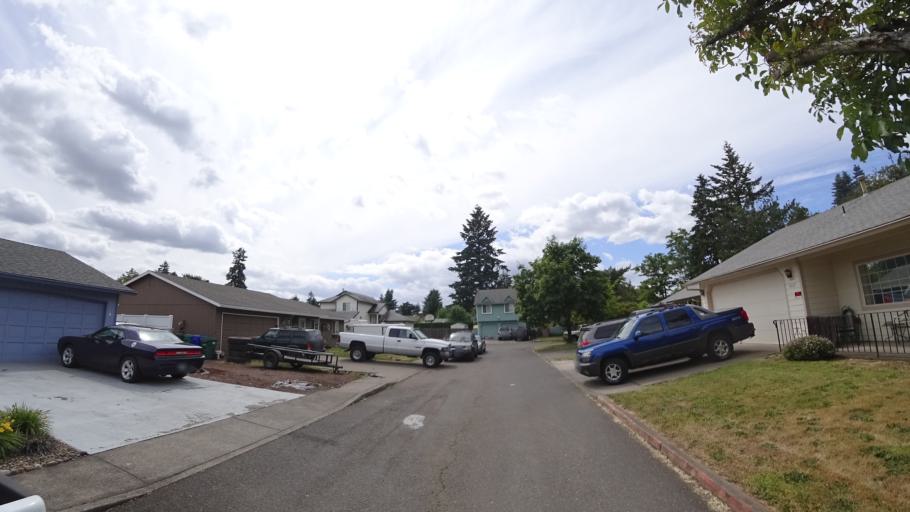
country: US
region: Oregon
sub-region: Multnomah County
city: Lents
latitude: 45.4843
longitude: -122.5498
